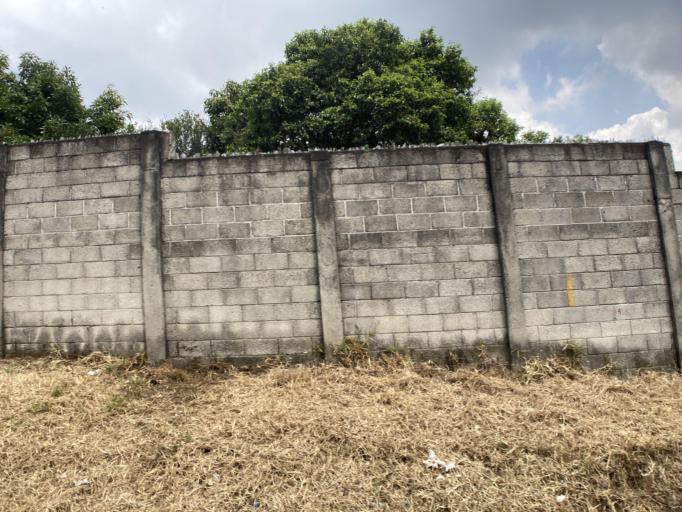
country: GT
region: Guatemala
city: Villa Canales
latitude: 14.4235
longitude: -90.5227
